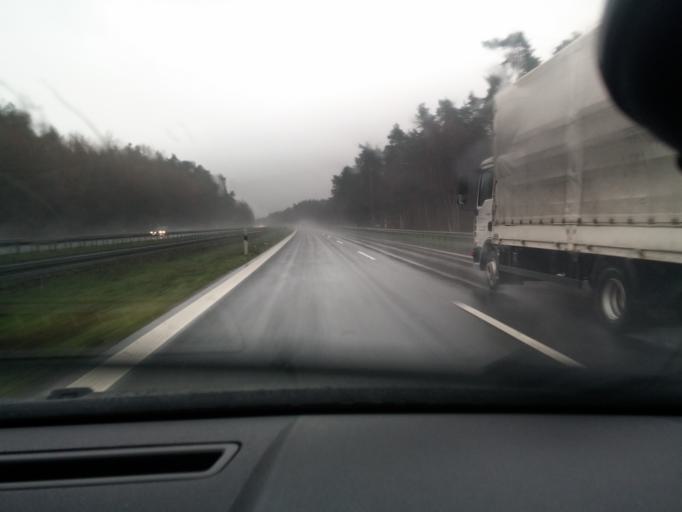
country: DE
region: Bavaria
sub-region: Regierungsbezirk Unterfranken
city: Kahl am Main
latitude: 50.0720
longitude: 9.0371
